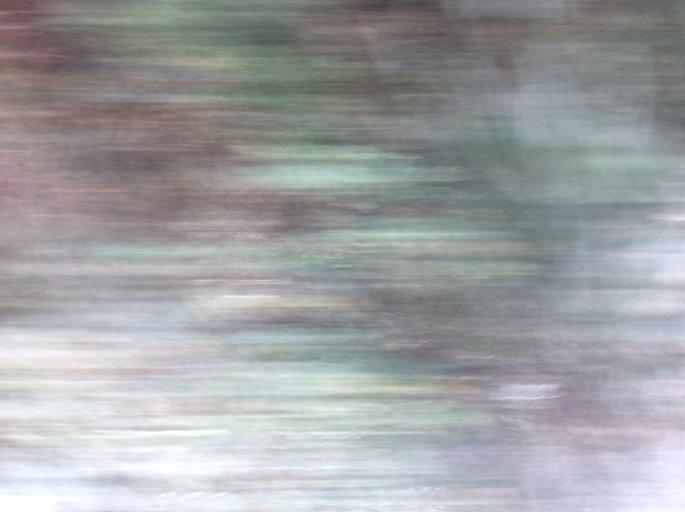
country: TW
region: Taipei
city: Taipei
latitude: 25.1780
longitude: 121.5449
